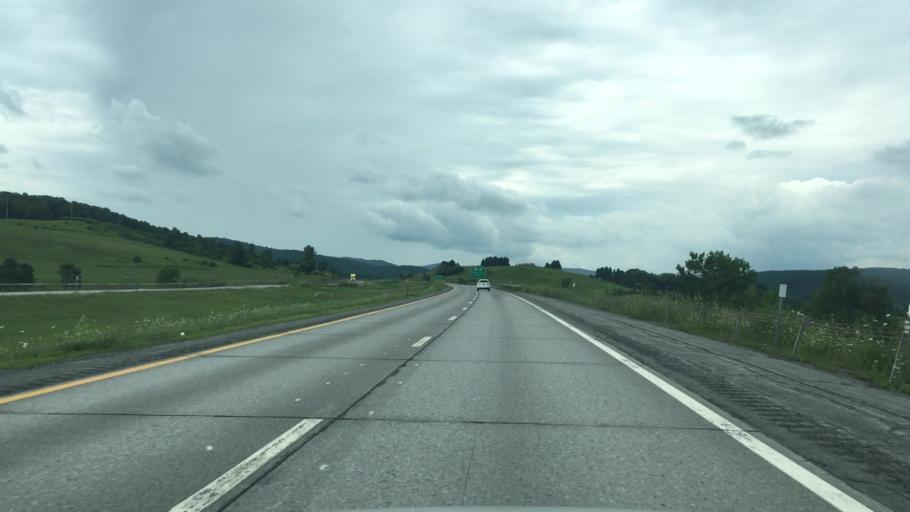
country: US
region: New York
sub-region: Schoharie County
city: Cobleskill
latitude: 42.6692
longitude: -74.4873
